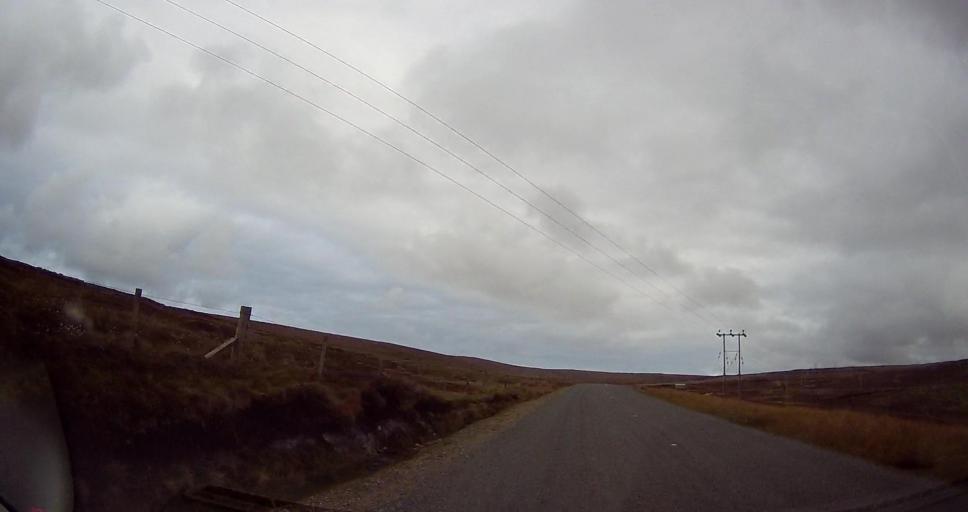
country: GB
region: Scotland
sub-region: Shetland Islands
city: Shetland
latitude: 60.6165
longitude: -1.0743
